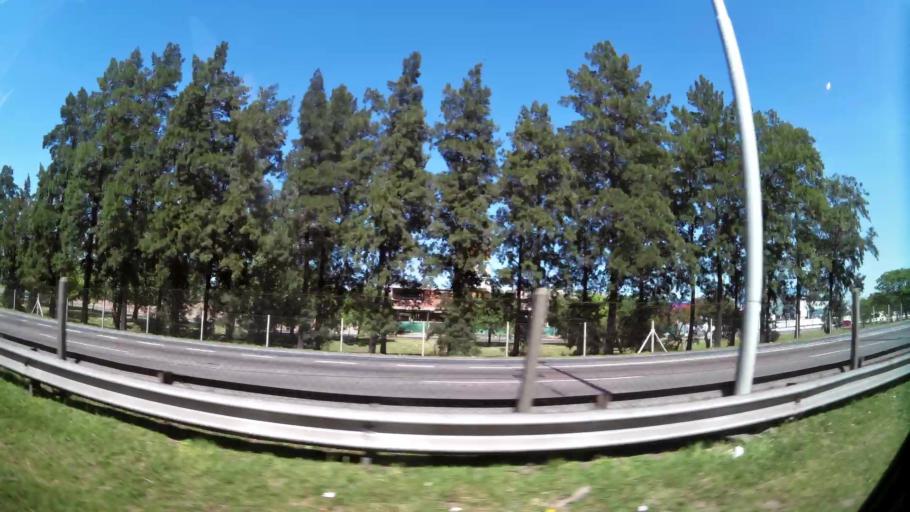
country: AR
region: Buenos Aires
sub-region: Partido de Tigre
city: Tigre
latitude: -34.4549
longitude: -58.5742
